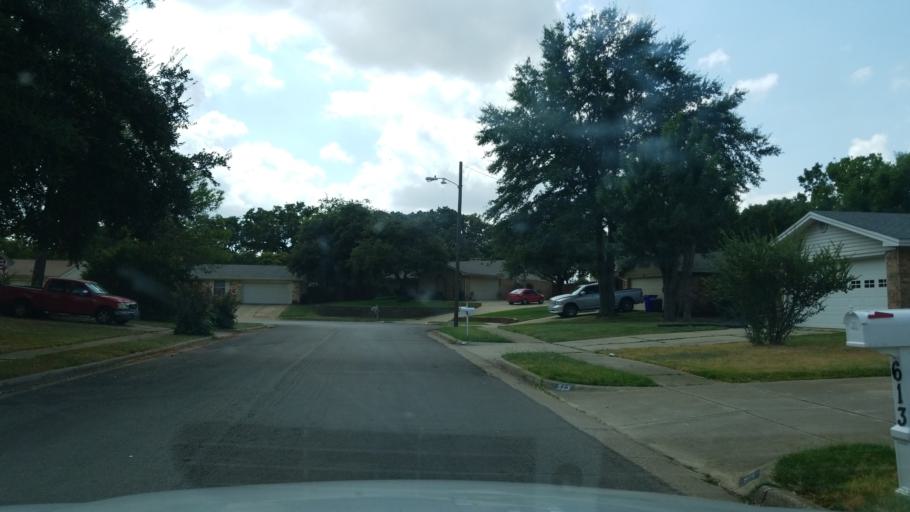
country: US
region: Texas
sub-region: Tarrant County
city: Euless
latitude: 32.8455
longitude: -97.0927
